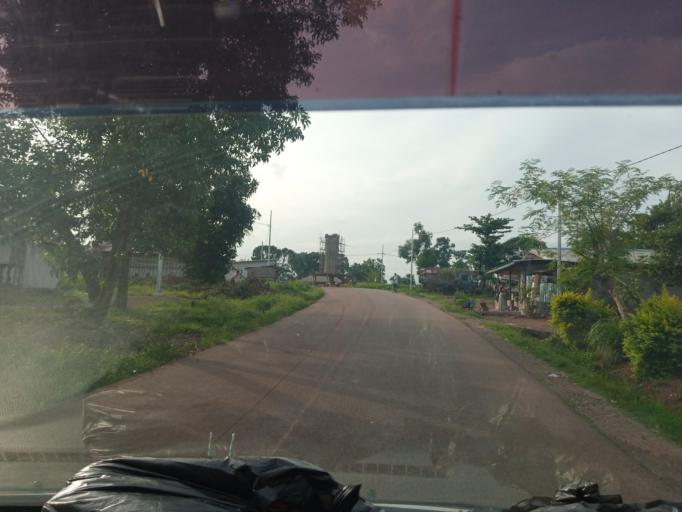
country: SL
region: Southern Province
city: Largo
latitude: 8.1995
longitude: -12.0593
